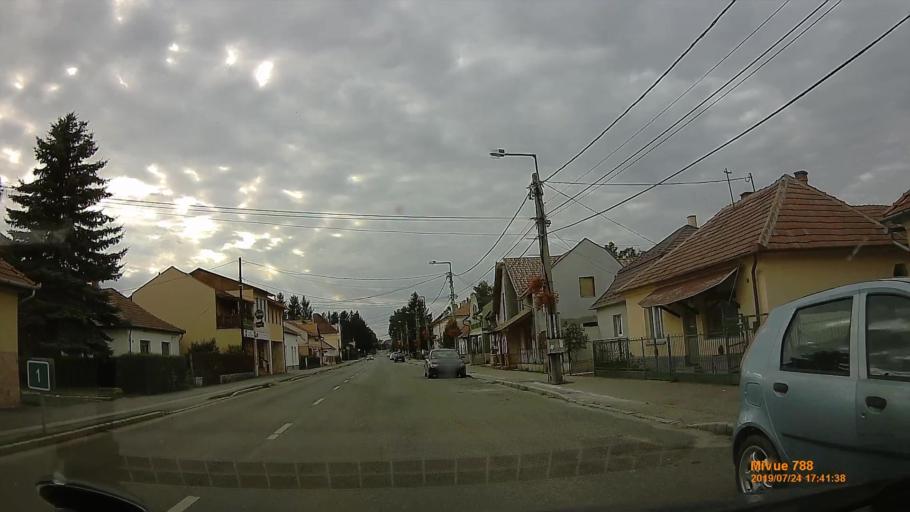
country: HU
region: Borsod-Abauj-Zemplen
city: Encs
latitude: 48.3319
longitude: 21.1185
